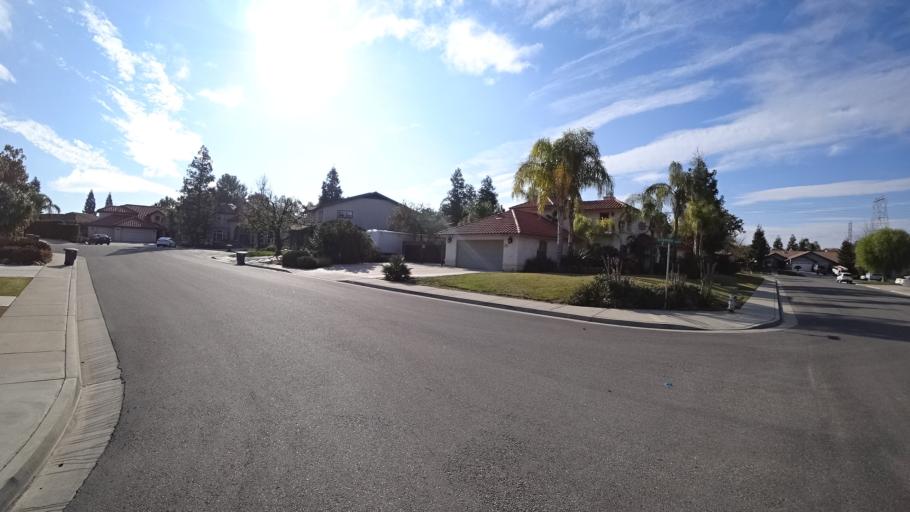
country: US
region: California
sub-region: Kern County
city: Oildale
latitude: 35.4027
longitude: -118.9183
